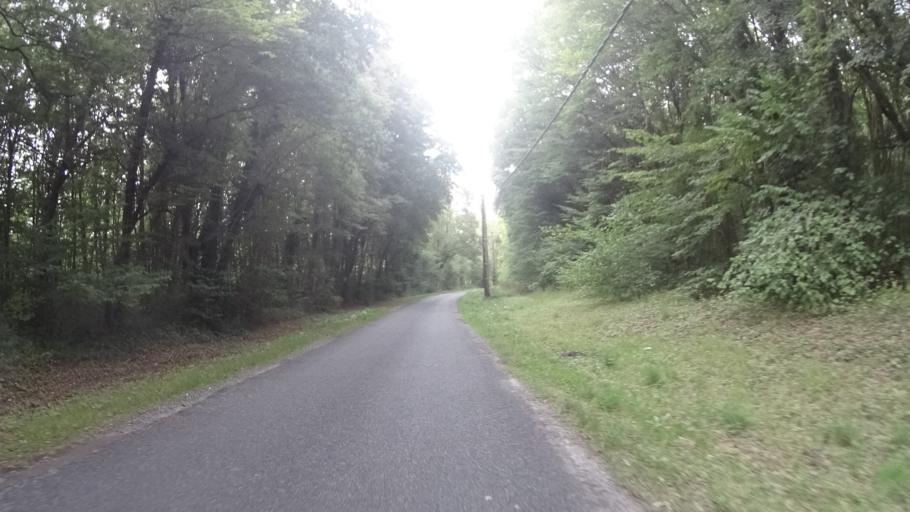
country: FR
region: Picardie
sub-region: Departement de l'Oise
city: Ver-sur-Launette
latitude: 49.1654
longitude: 2.6796
